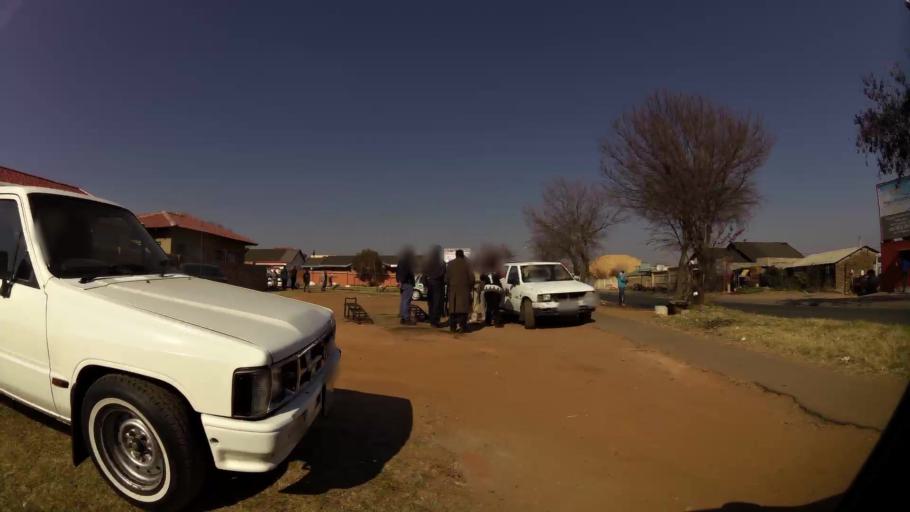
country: ZA
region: Gauteng
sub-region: City of Johannesburg Metropolitan Municipality
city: Johannesburg
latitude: -26.2460
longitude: 27.9550
